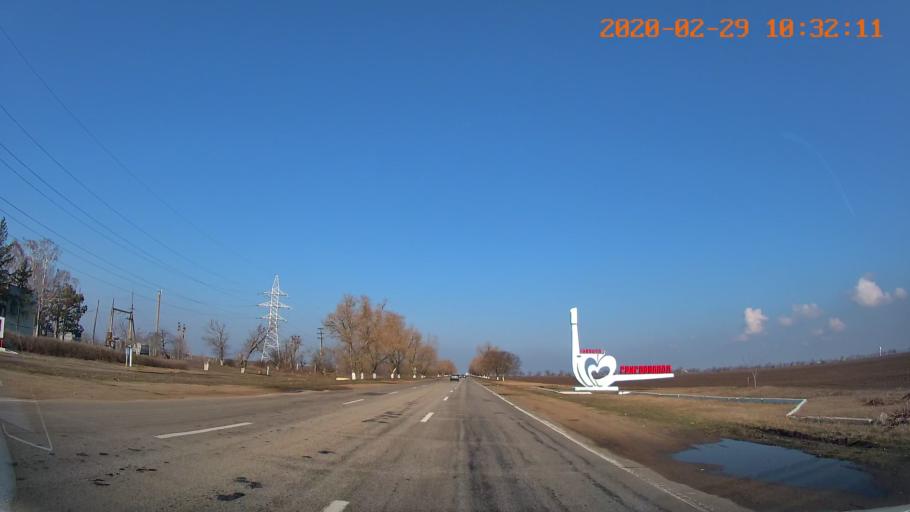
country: UA
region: Odessa
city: Velykoploske
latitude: 46.9580
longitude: 29.5559
